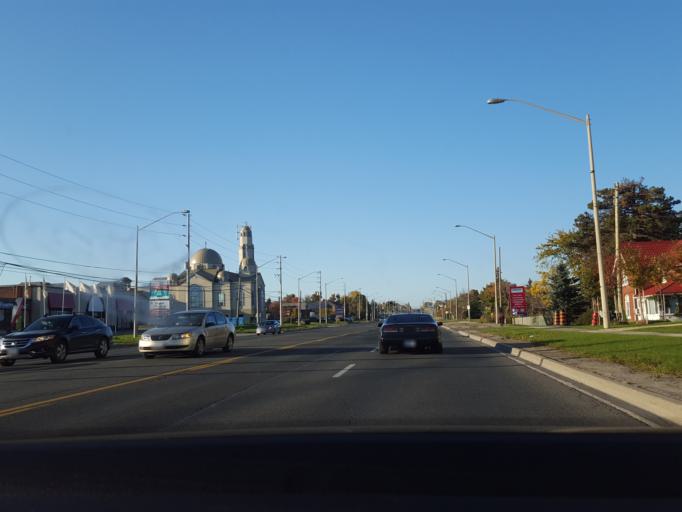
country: CA
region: Ontario
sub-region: York
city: Richmond Hill
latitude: 43.9021
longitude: -79.4443
